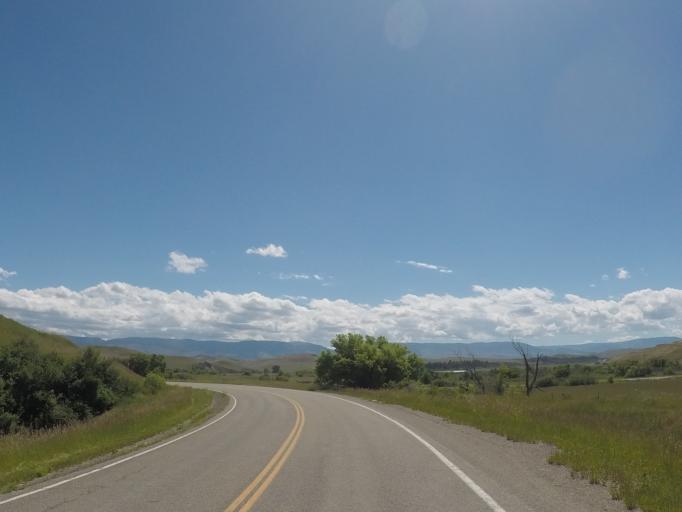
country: US
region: Wyoming
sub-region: Sheridan County
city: Sheridan
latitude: 45.0564
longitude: -107.3526
